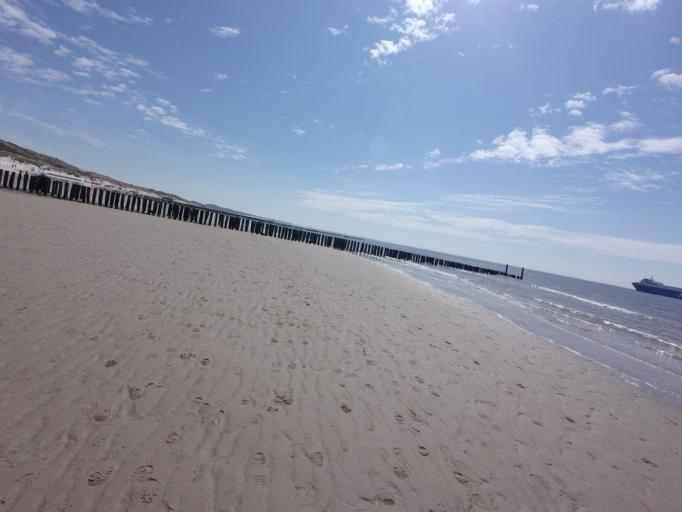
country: NL
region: Zeeland
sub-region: Gemeente Vlissingen
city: Vlissingen
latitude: 51.5081
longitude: 3.4616
